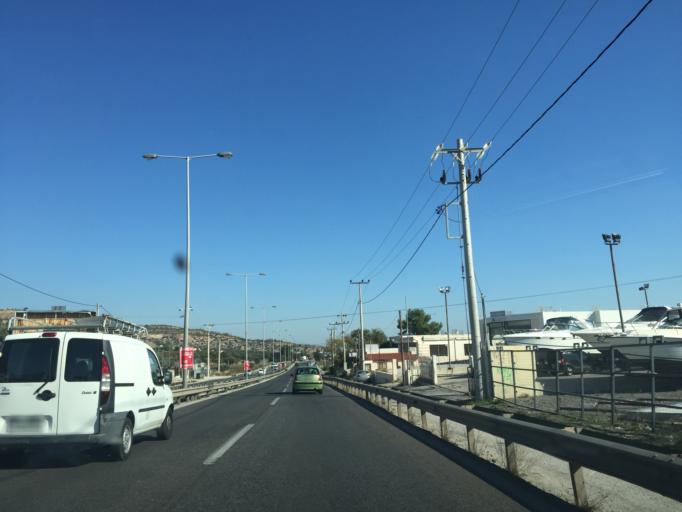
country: GR
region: Attica
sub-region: Nomarchia Anatolikis Attikis
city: Kitsi
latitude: 37.8659
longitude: 23.8514
